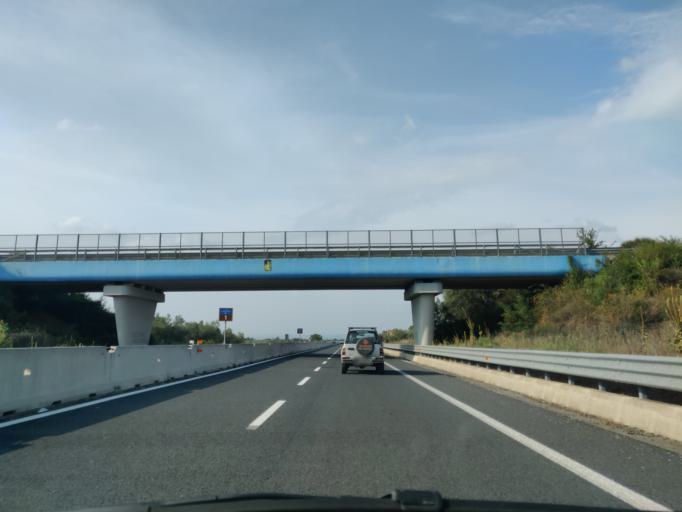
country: IT
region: Latium
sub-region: Provincia di Viterbo
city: Blera
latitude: 42.3153
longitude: 11.9917
